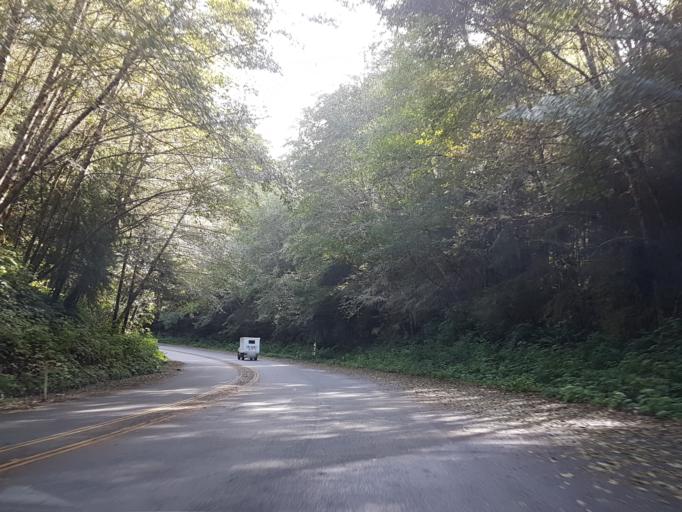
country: US
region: California
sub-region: Del Norte County
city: Bertsch-Oceanview
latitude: 41.4598
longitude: -124.0476
